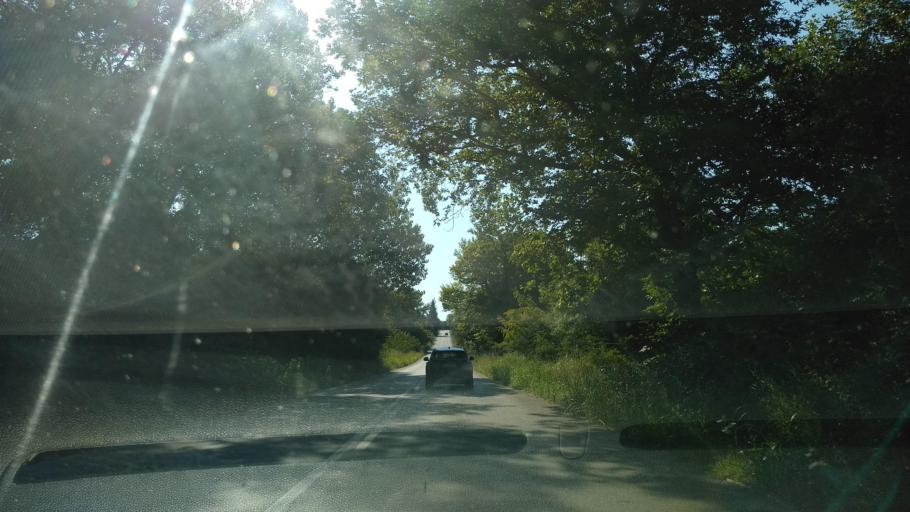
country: GR
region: Central Macedonia
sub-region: Nomos Chalkidikis
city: Ierissos
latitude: 40.4392
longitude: 23.8325
